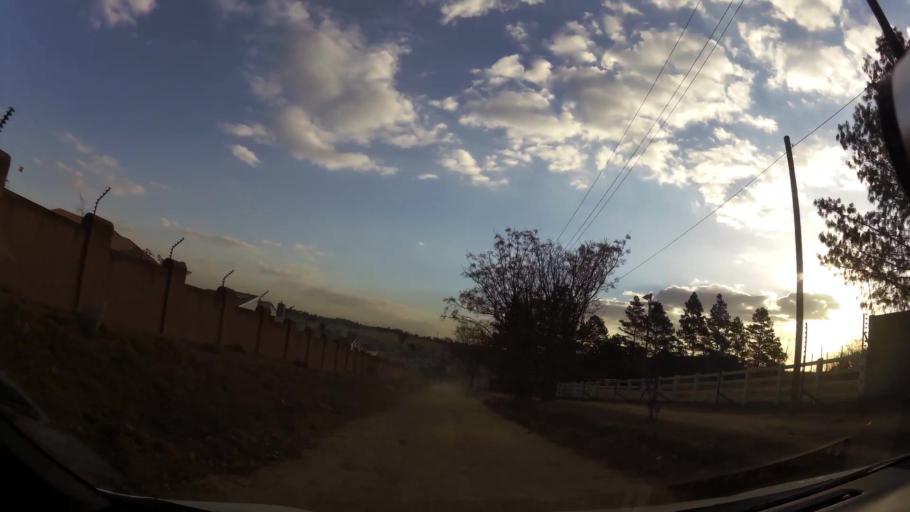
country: ZA
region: Gauteng
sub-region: City of Johannesburg Metropolitan Municipality
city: Diepsloot
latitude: -26.0055
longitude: 27.9730
